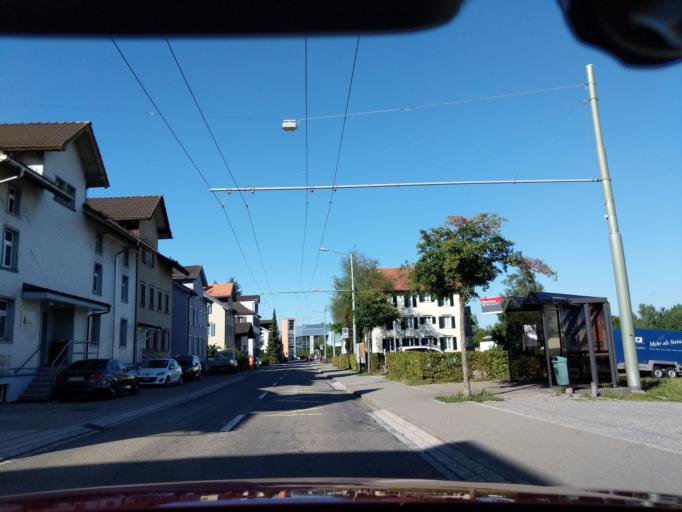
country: CH
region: Appenzell Ausserrhoden
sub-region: Bezirk Hinterland
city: Herisau
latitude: 47.4046
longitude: 9.3032
